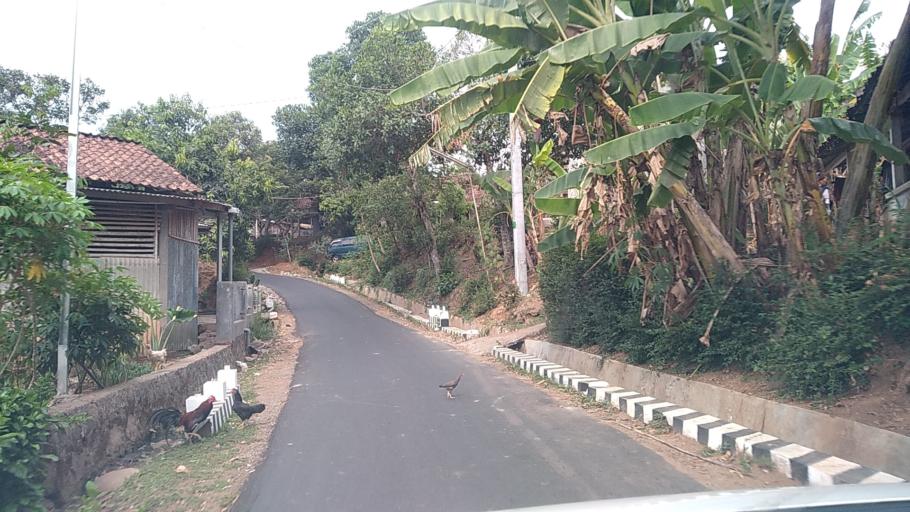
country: ID
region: Central Java
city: Ungaran
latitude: -7.1100
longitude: 110.3831
